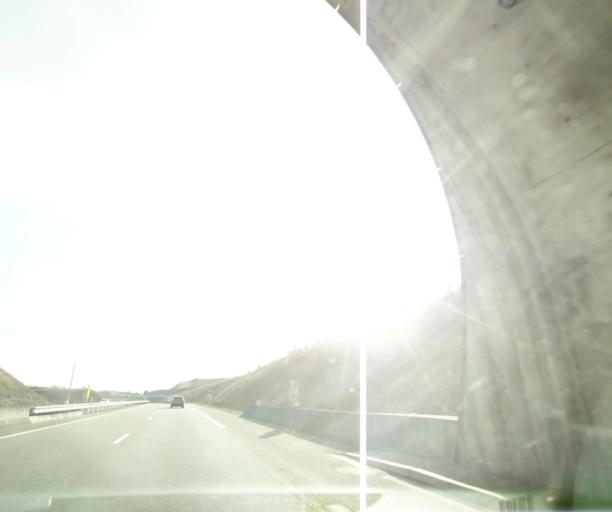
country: FR
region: Midi-Pyrenees
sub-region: Departement du Lot
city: Cahors
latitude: 44.4987
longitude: 1.4940
